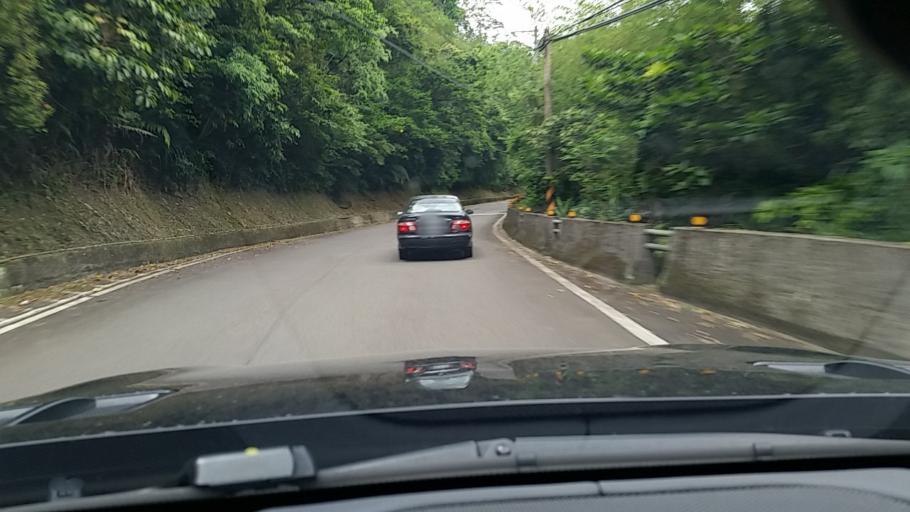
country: TW
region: Taiwan
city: Daxi
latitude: 24.7972
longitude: 121.3019
